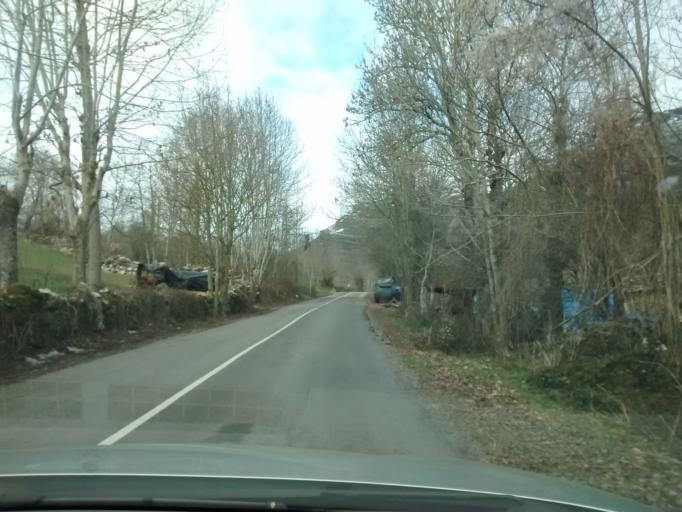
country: ES
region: Castille and Leon
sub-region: Provincia de Burgos
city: Espinosa de los Monteros
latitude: 43.1223
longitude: -3.6056
